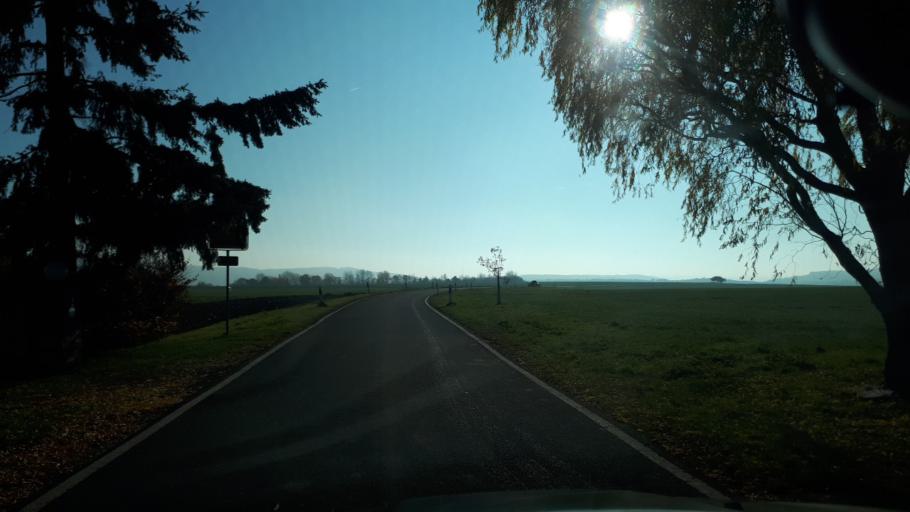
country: DE
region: Rheinland-Pfalz
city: Brieden
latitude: 50.1855
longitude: 7.2647
